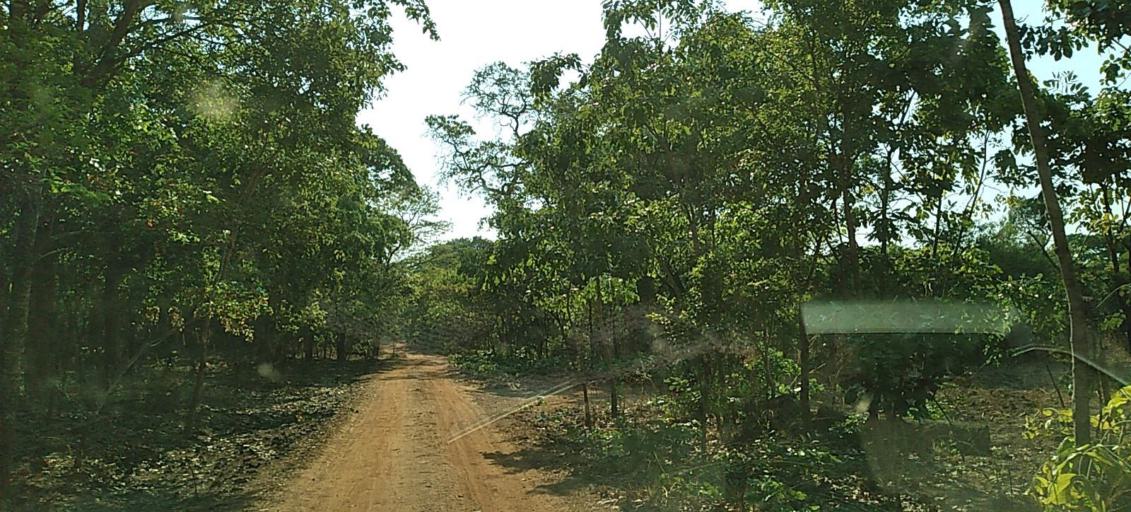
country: ZM
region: Copperbelt
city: Kalulushi
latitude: -13.0049
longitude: 27.7565
